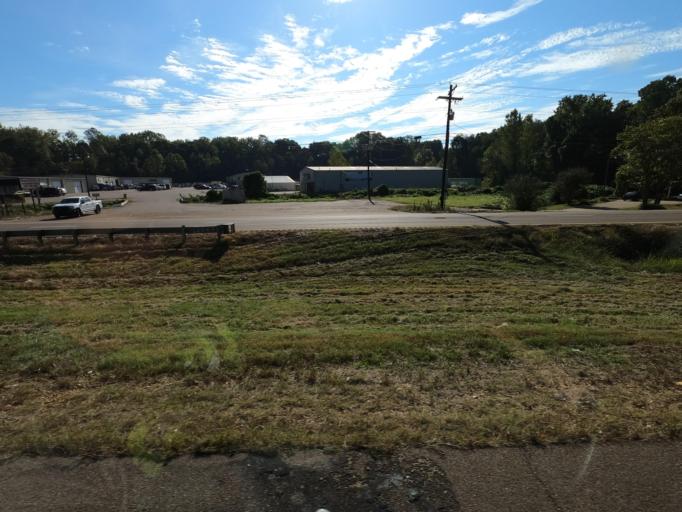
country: US
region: Tennessee
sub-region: Tipton County
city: Munford
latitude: 35.4265
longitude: -89.8122
